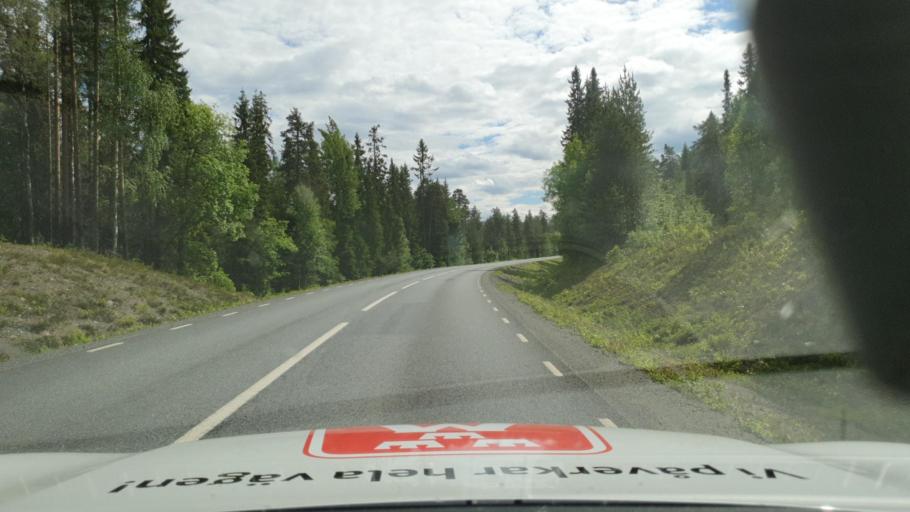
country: SE
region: Vaesterbotten
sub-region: Norsjo Kommun
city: Norsjoe
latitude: 65.0088
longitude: 19.4194
